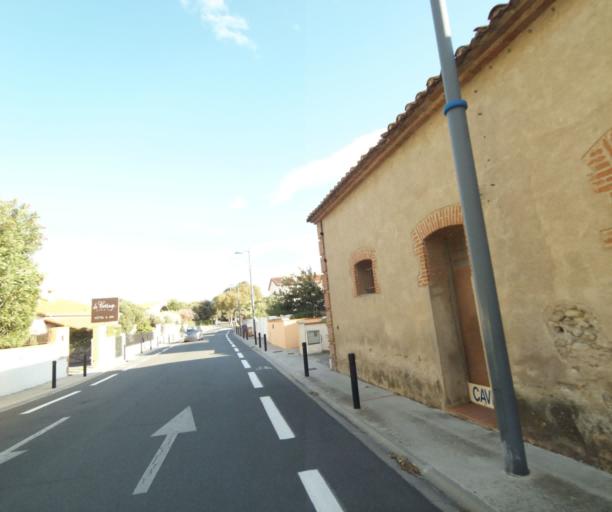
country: FR
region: Languedoc-Roussillon
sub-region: Departement des Pyrenees-Orientales
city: Argelers
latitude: 42.5464
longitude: 3.0287
